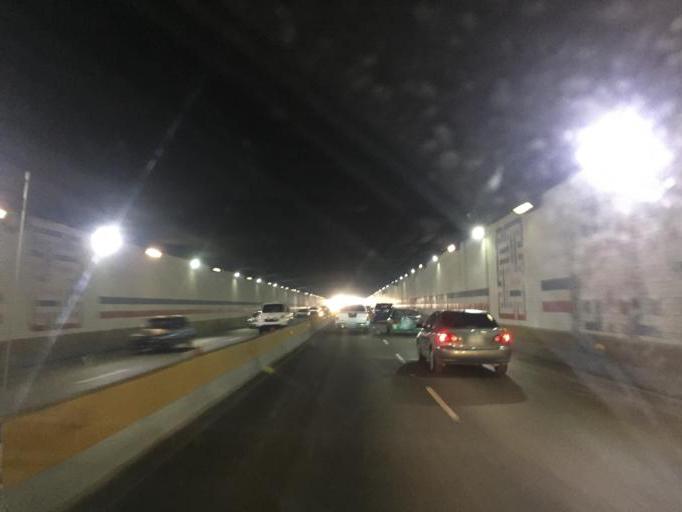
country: DO
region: Nacional
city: La Julia
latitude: 18.4624
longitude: -69.9366
